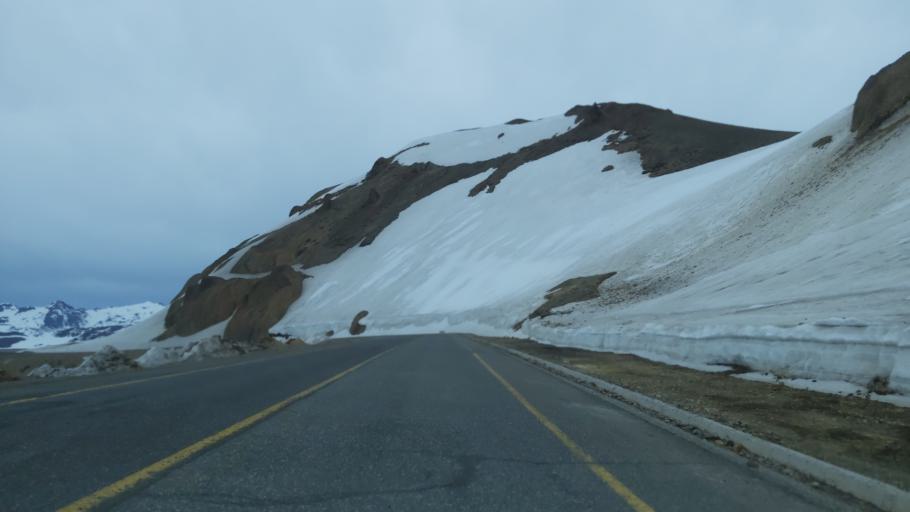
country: CL
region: Maule
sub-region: Provincia de Linares
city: Colbun
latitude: -36.0145
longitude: -70.5142
